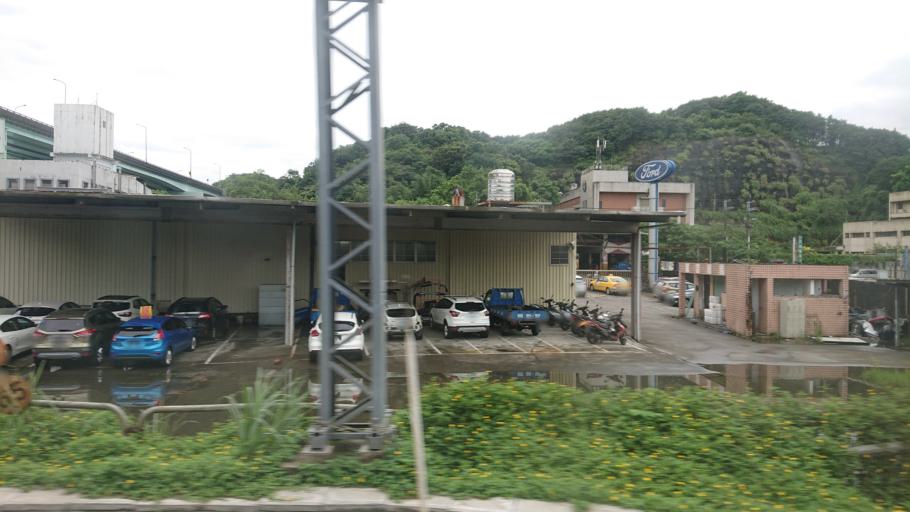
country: TW
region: Taiwan
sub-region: Keelung
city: Keelung
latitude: 25.1043
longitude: 121.7256
